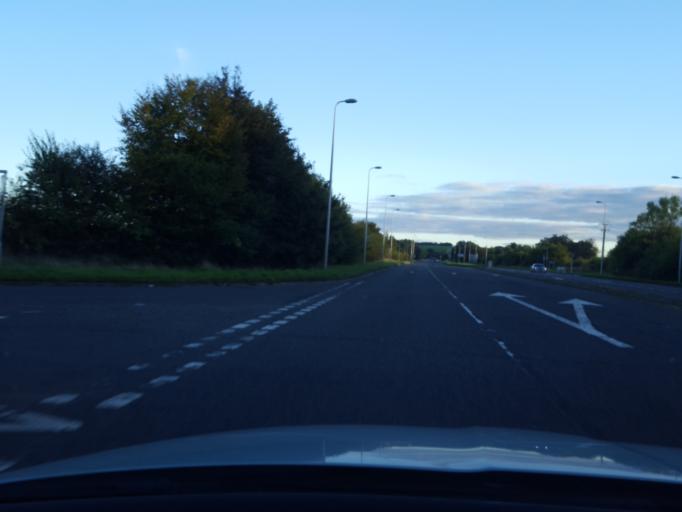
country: GB
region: Scotland
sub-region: West Lothian
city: Bathgate
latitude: 55.9200
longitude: -3.6784
